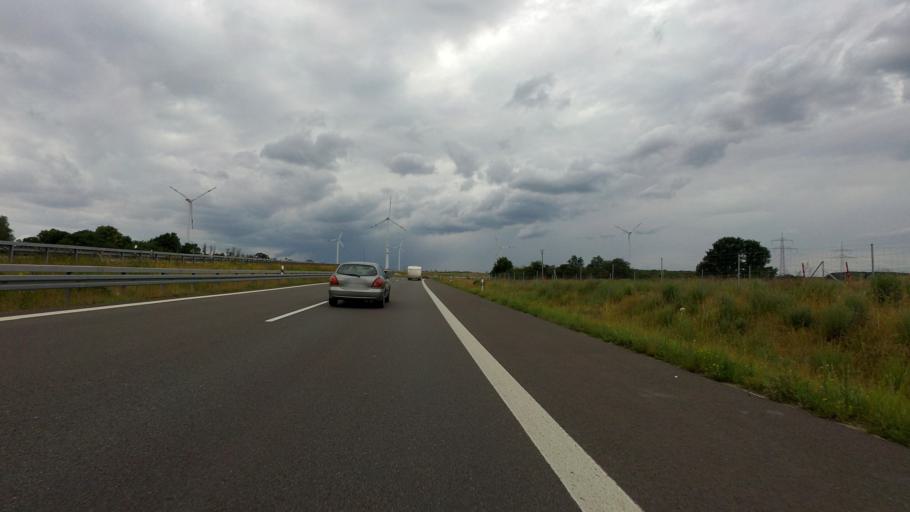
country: DE
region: Brandenburg
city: Ahrensfelde
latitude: 52.6170
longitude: 13.5547
